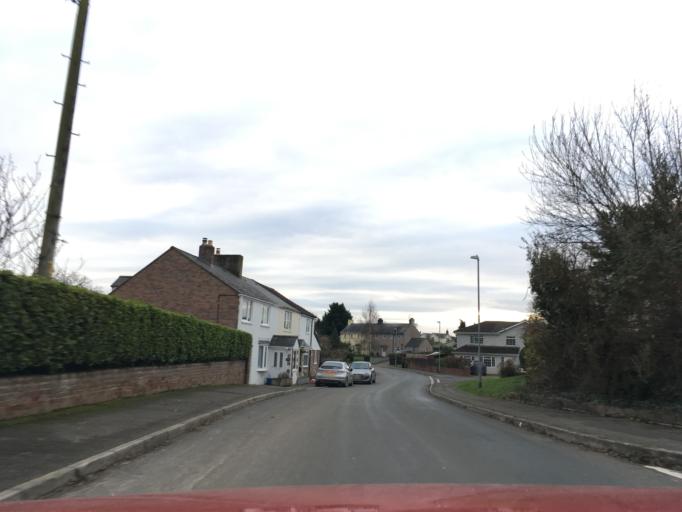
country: GB
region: Wales
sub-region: Monmouthshire
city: Magor
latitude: 51.5850
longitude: -2.8335
